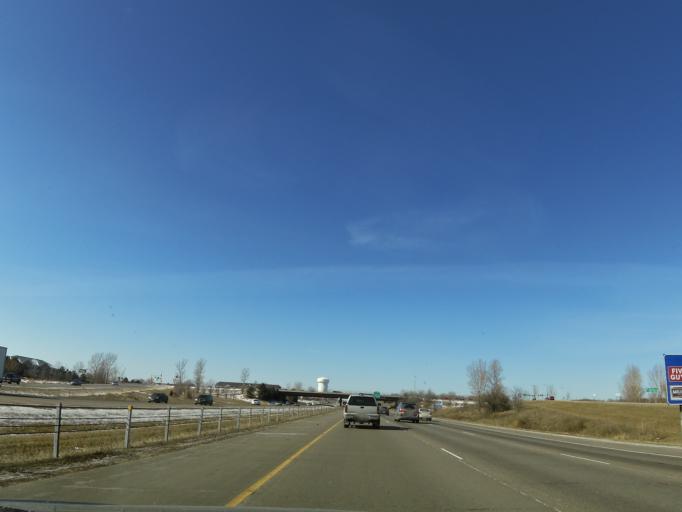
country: US
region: Minnesota
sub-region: Washington County
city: Lake Elmo
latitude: 44.9487
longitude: -92.8987
